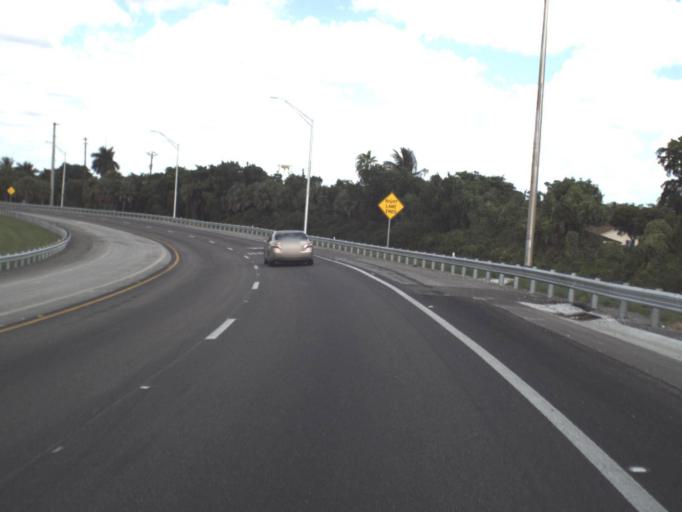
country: US
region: Florida
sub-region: Broward County
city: Miramar
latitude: 25.9750
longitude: -80.2284
